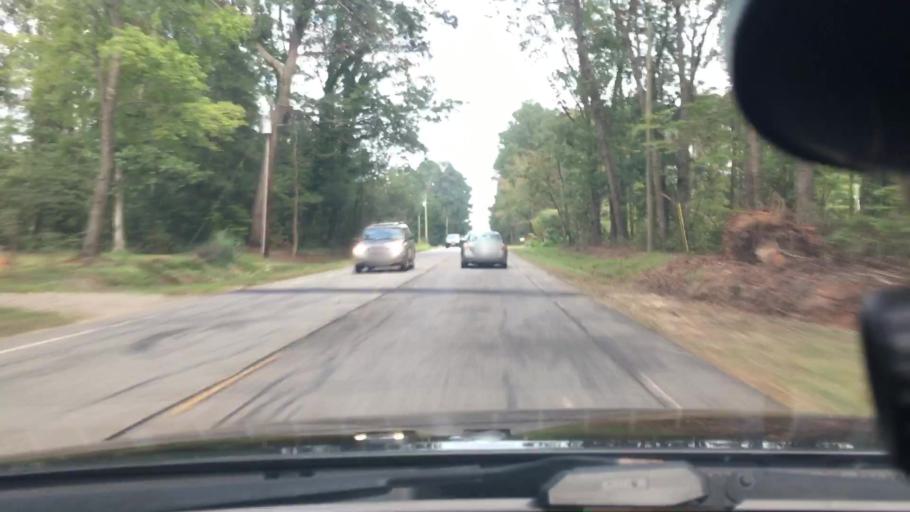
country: US
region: North Carolina
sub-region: Moore County
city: Carthage
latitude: 35.3574
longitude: -79.3362
